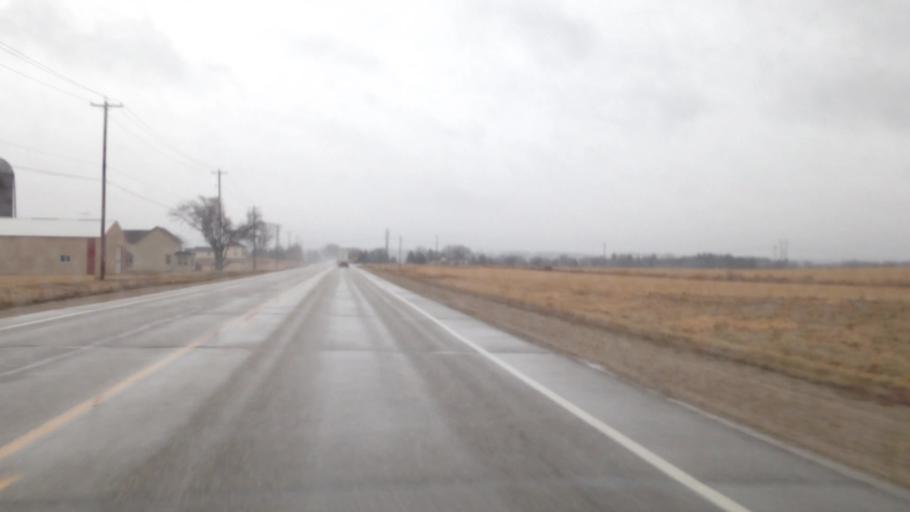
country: US
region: Wisconsin
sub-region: Washington County
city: Hartford
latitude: 43.4214
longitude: -88.3653
